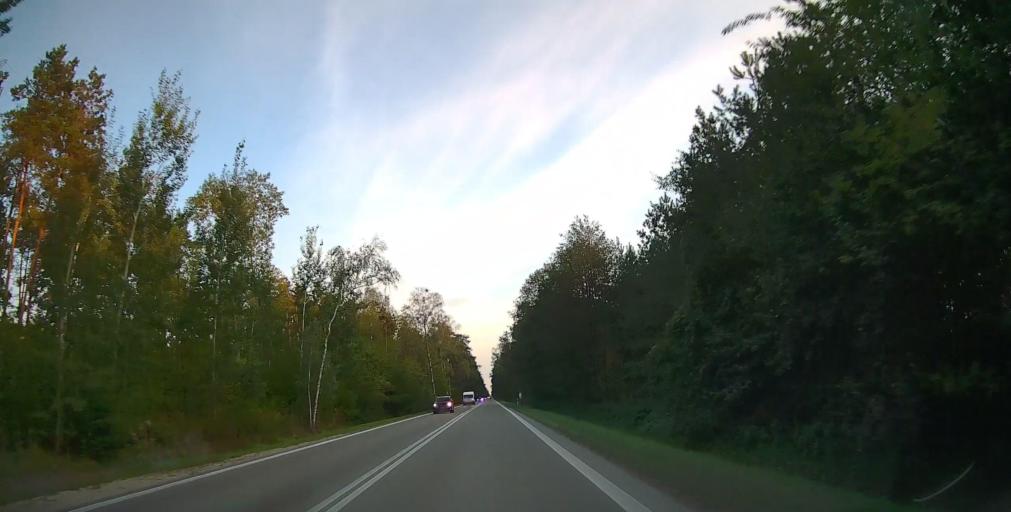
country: PL
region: Masovian Voivodeship
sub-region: Powiat kozienicki
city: Ryczywol
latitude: 51.6636
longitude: 21.4464
